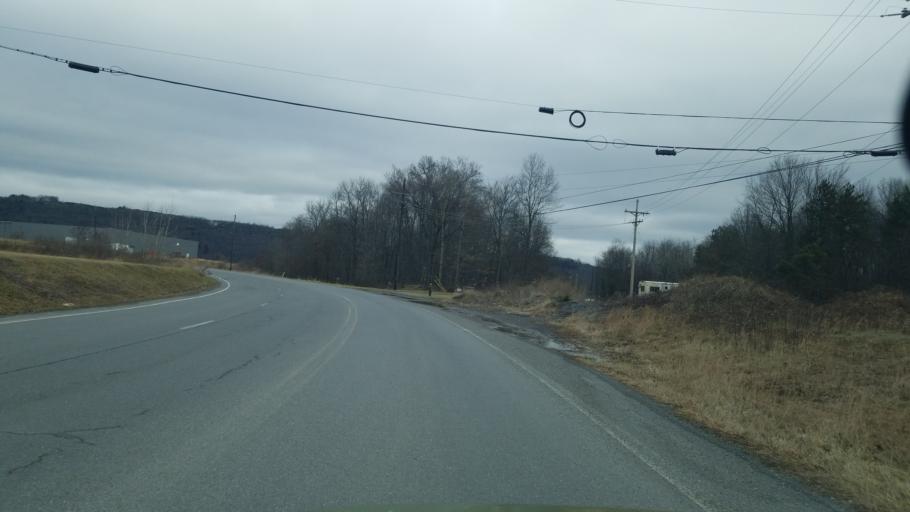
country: US
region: Pennsylvania
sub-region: Clearfield County
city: Clearfield
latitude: 41.0287
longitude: -78.3887
